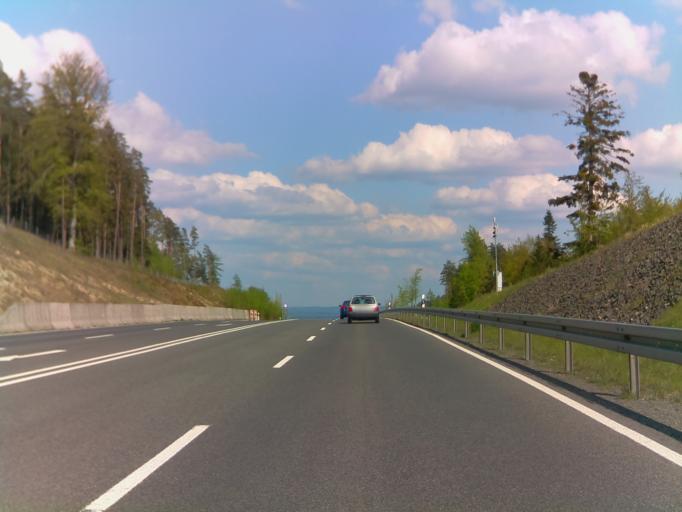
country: DE
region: Bavaria
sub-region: Upper Franconia
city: Rodental
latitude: 50.3054
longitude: 11.0450
